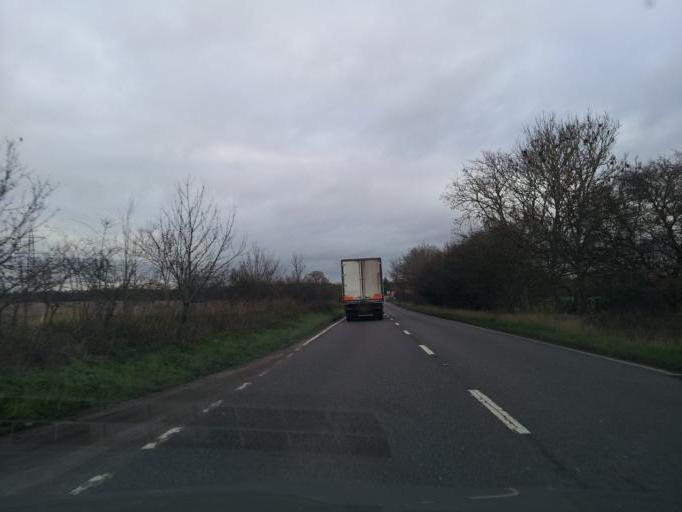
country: GB
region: England
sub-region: Norfolk
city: Diss
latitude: 52.3546
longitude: 1.1414
